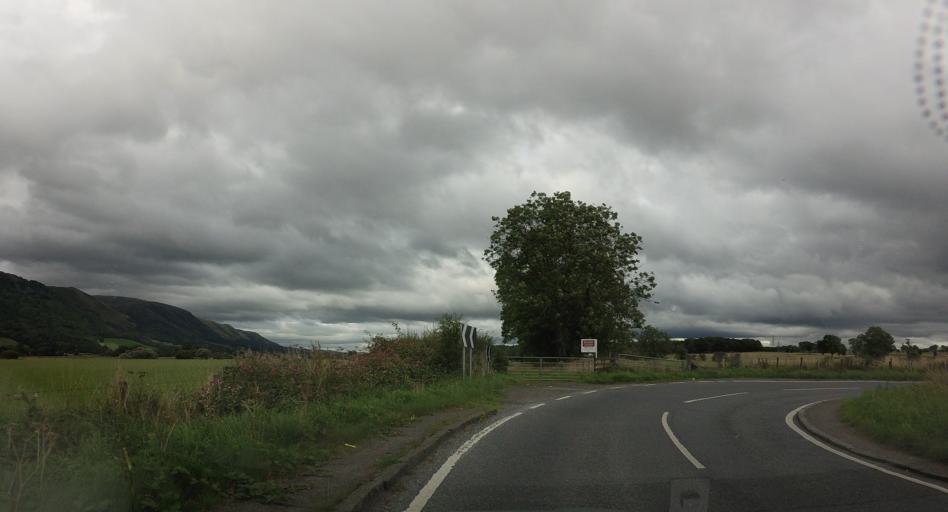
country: GB
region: Scotland
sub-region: Clackmannanshire
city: Alva
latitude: 56.1429
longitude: -3.7962
